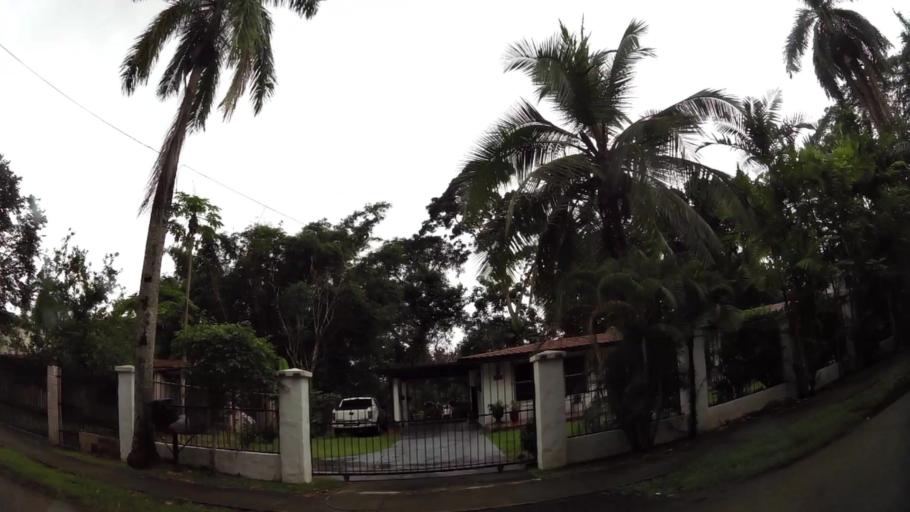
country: PA
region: Panama
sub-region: Distrito de Panama
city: Ancon
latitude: 9.0026
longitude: -79.5741
